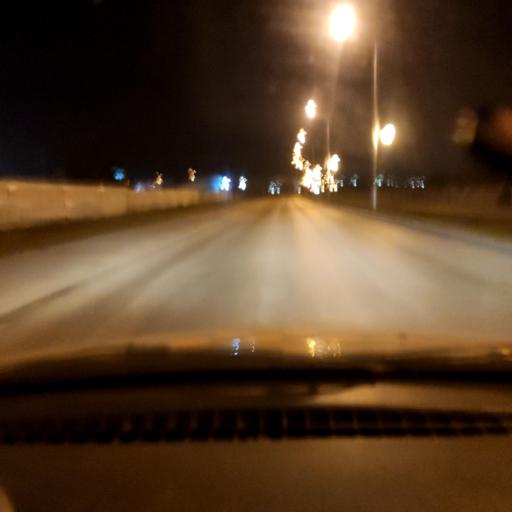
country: RU
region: Bashkortostan
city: Ufa
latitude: 54.7805
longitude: 56.0778
